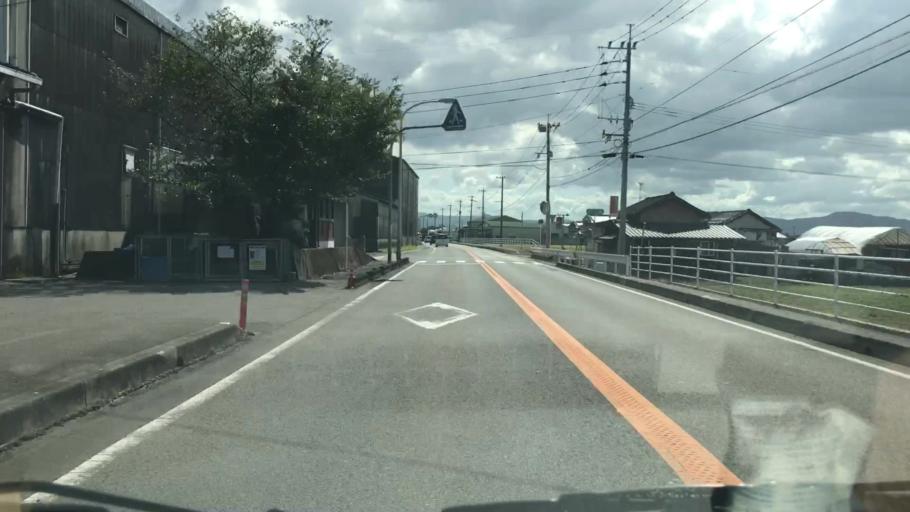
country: JP
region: Saga Prefecture
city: Kashima
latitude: 33.1779
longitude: 130.1858
